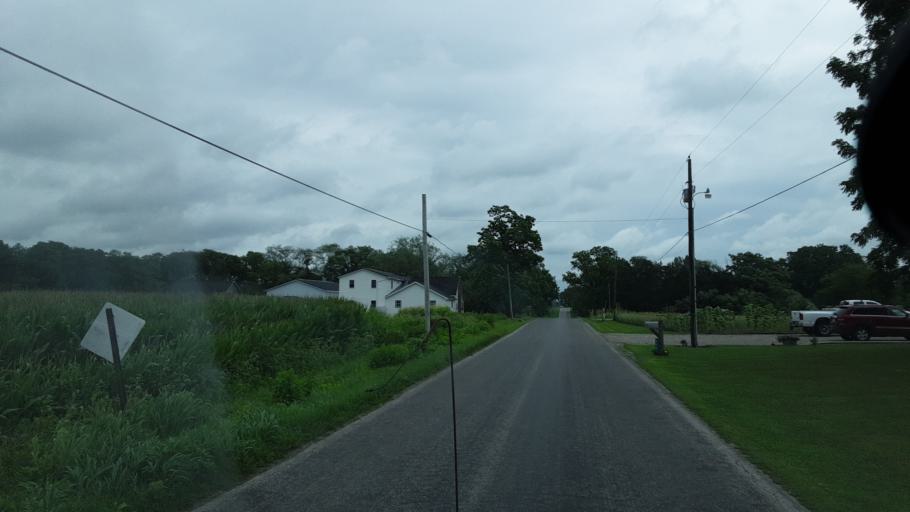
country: US
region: Indiana
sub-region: Adams County
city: Geneva
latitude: 40.5331
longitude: -84.9965
